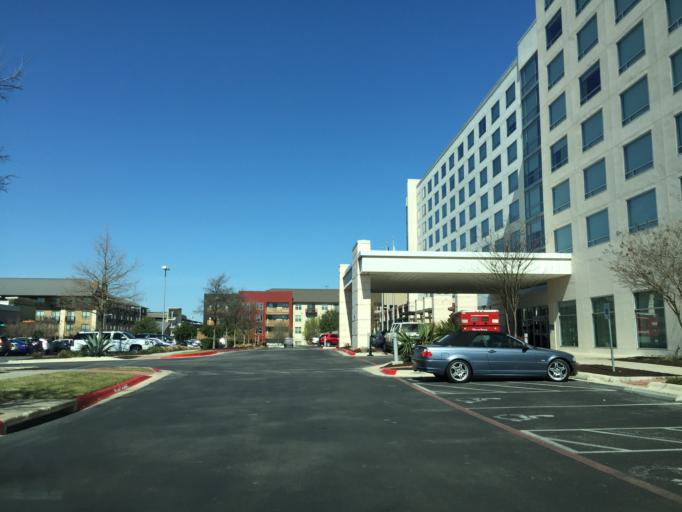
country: US
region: Texas
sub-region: Travis County
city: Wells Branch
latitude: 30.3989
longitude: -97.7252
